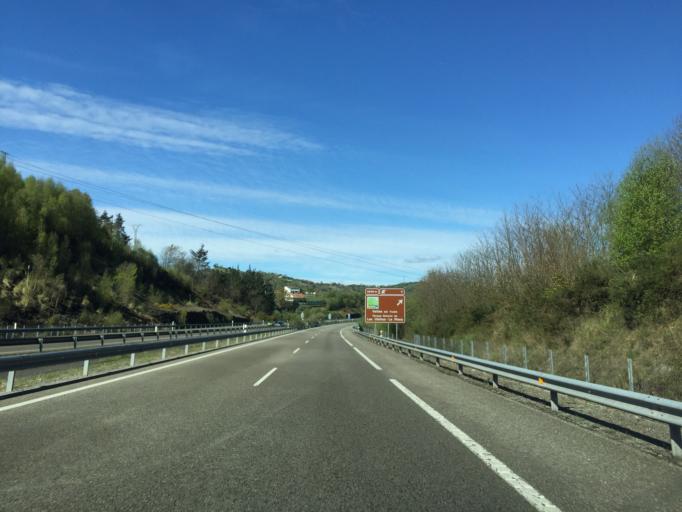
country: ES
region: Asturias
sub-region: Province of Asturias
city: Oviedo
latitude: 43.3528
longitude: -5.9224
